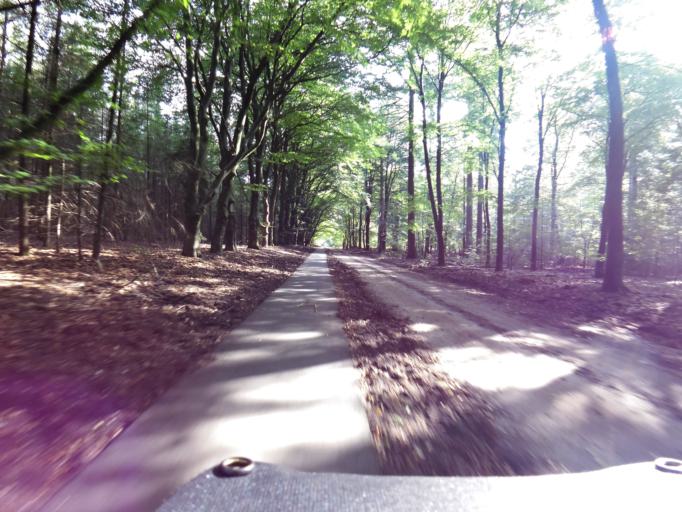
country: NL
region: Gelderland
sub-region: Gemeente Apeldoorn
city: Uddel
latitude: 52.2108
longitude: 5.8096
